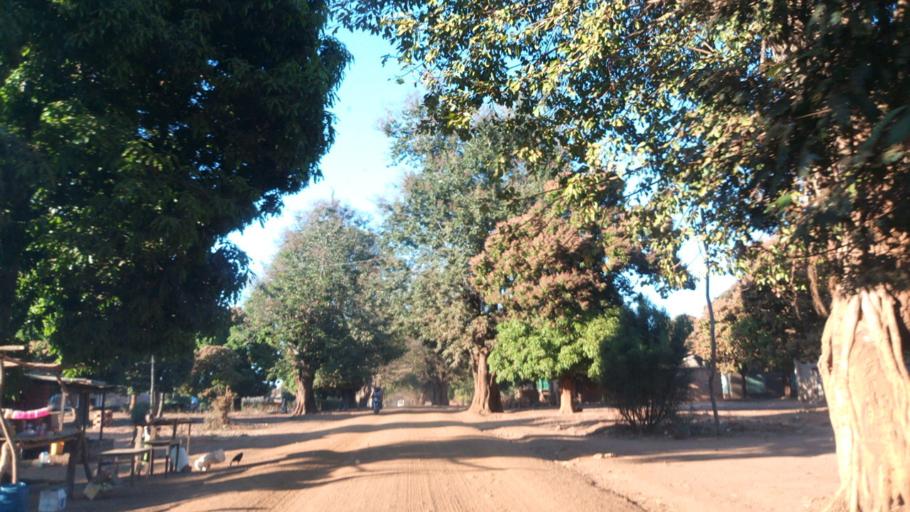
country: ZM
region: Luapula
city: Mwense
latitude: -10.3872
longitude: 28.6163
